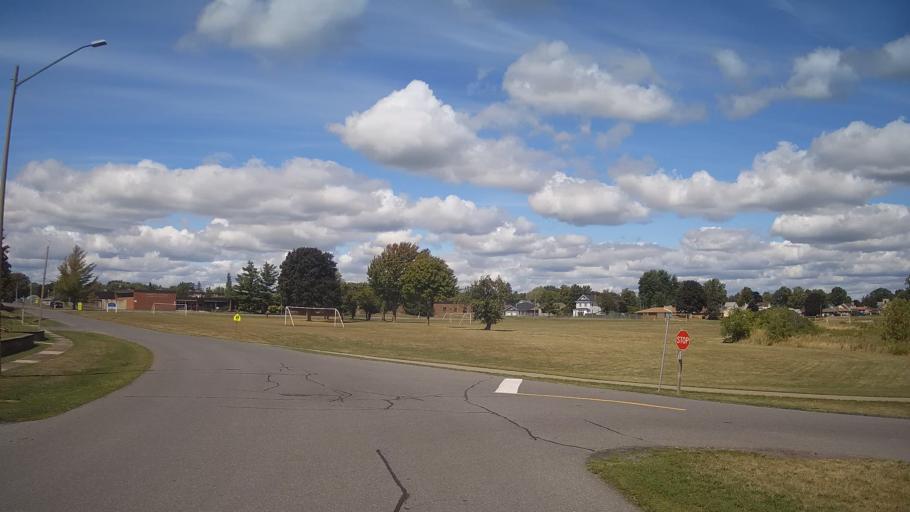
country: US
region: New York
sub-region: St. Lawrence County
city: Ogdensburg
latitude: 44.8470
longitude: -75.3123
